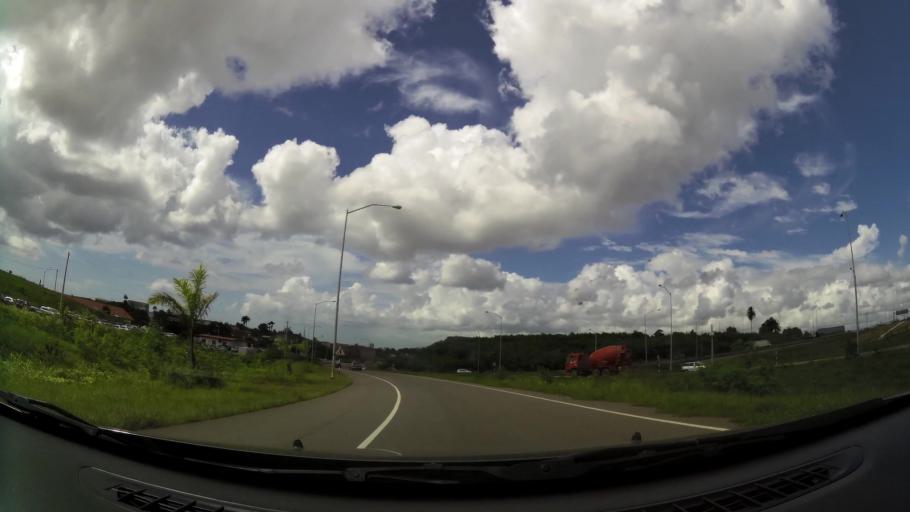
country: TT
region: City of San Fernando
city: Mon Repos
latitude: 10.2529
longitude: -61.4414
